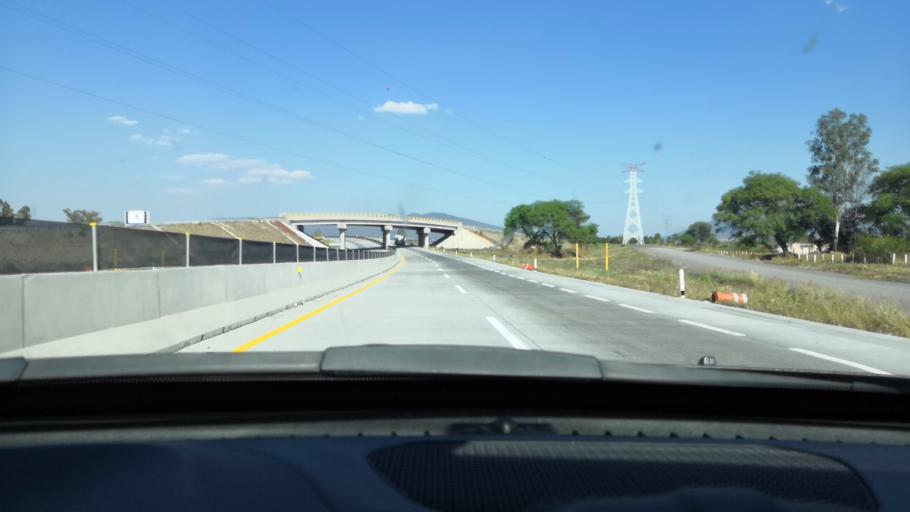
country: MX
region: Jalisco
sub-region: Ixtlahuacan de los Membrillos
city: Los Cedros
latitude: 20.4096
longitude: -103.2187
